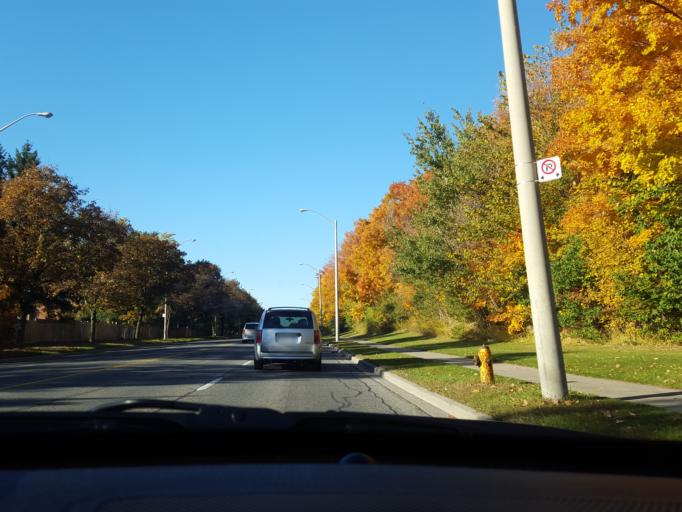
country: CA
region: Ontario
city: Scarborough
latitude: 43.8073
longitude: -79.2780
